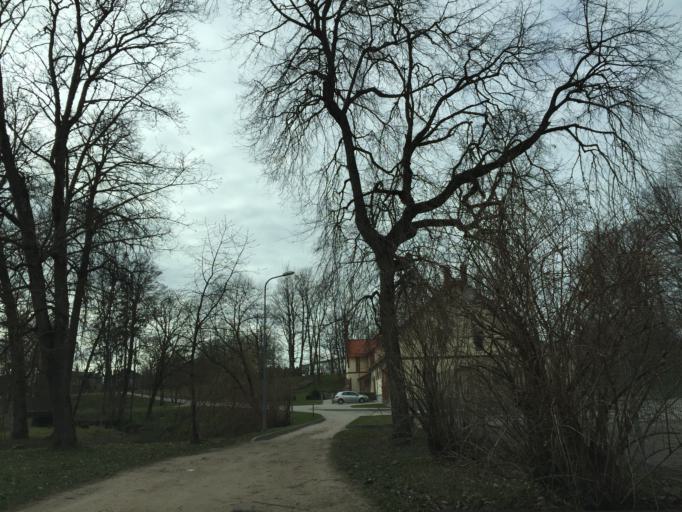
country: LT
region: Klaipedos apskritis
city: Gargzdai
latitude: 55.7160
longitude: 21.4747
